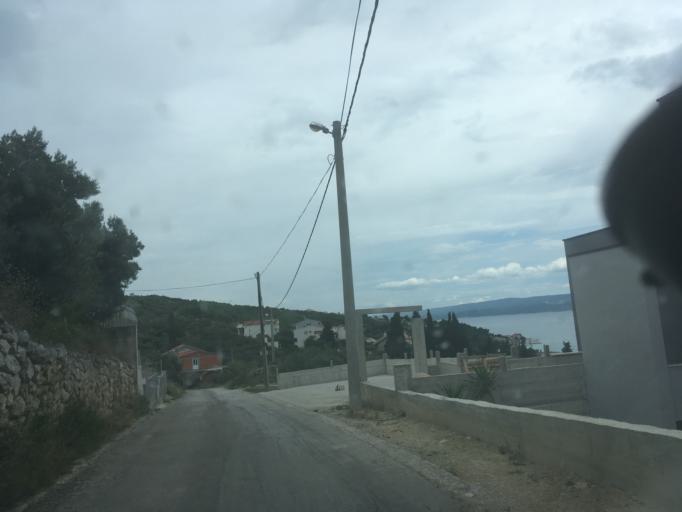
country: HR
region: Splitsko-Dalmatinska
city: Jesenice
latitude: 43.4558
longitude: 16.6221
